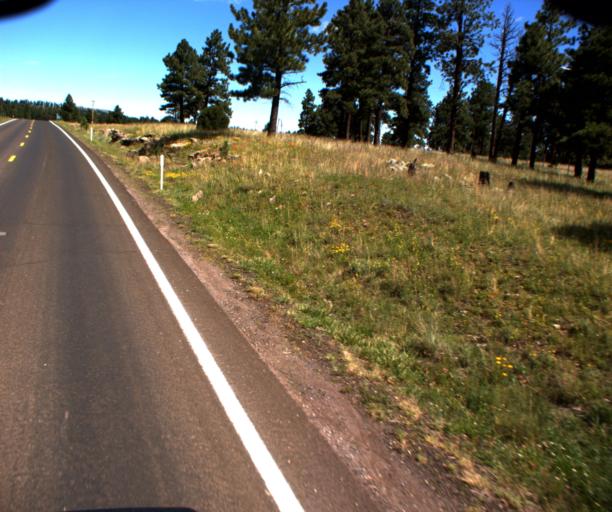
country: US
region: Arizona
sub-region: Apache County
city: Eagar
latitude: 34.0278
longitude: -109.4504
